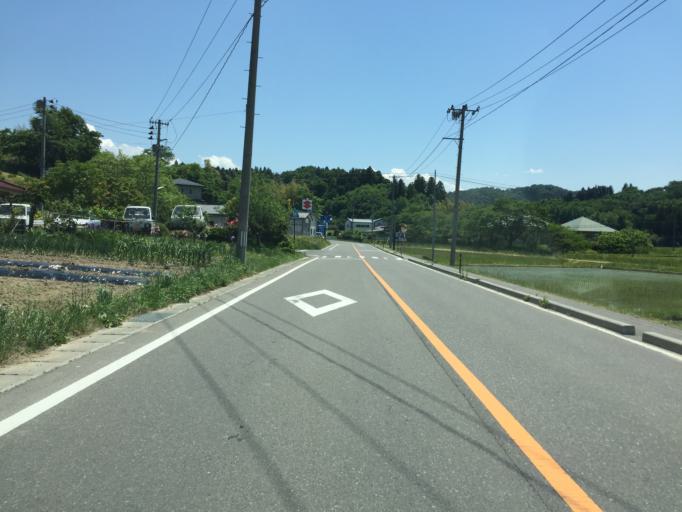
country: JP
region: Fukushima
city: Motomiya
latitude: 37.5001
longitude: 140.4632
